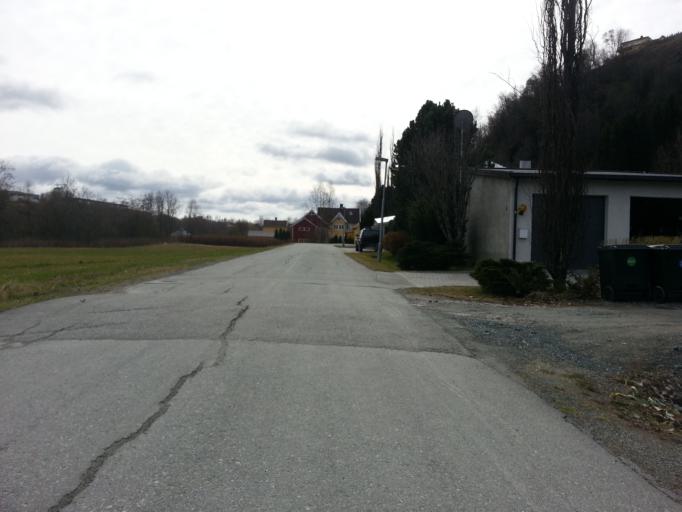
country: NO
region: Sor-Trondelag
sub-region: Trondheim
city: Trondheim
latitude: 63.4052
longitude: 10.3877
